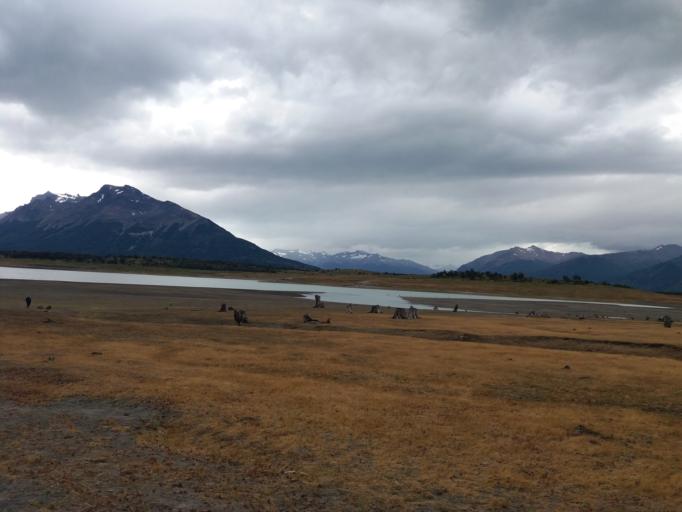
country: AR
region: Santa Cruz
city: El Calafate
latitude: -50.5544
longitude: -72.8507
